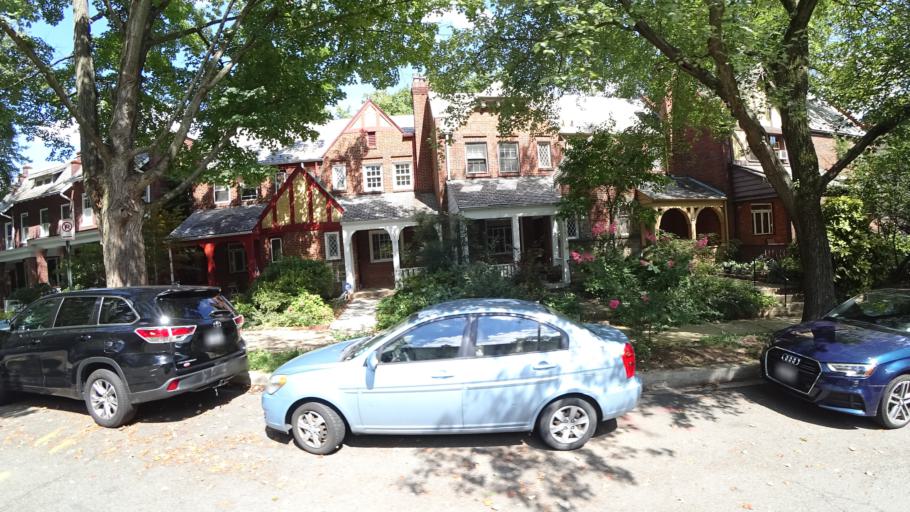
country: US
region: Washington, D.C.
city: Washington, D.C.
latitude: 38.9333
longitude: -77.0467
